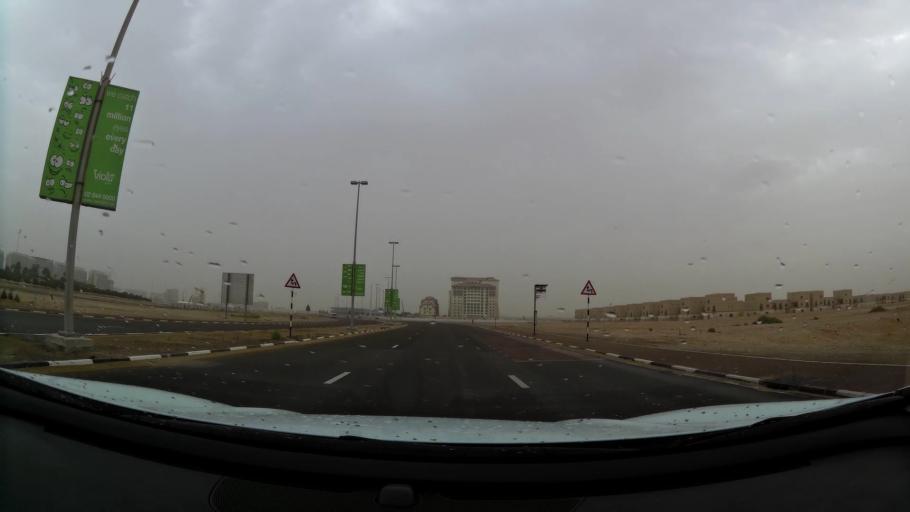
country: AE
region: Abu Dhabi
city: Abu Dhabi
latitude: 24.4416
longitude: 54.6024
